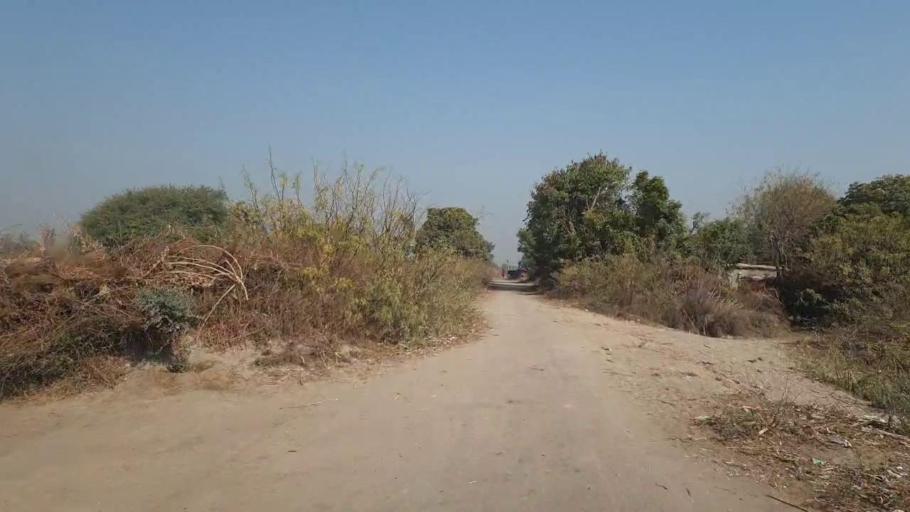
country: PK
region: Sindh
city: Tando Allahyar
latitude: 25.3775
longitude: 68.6458
